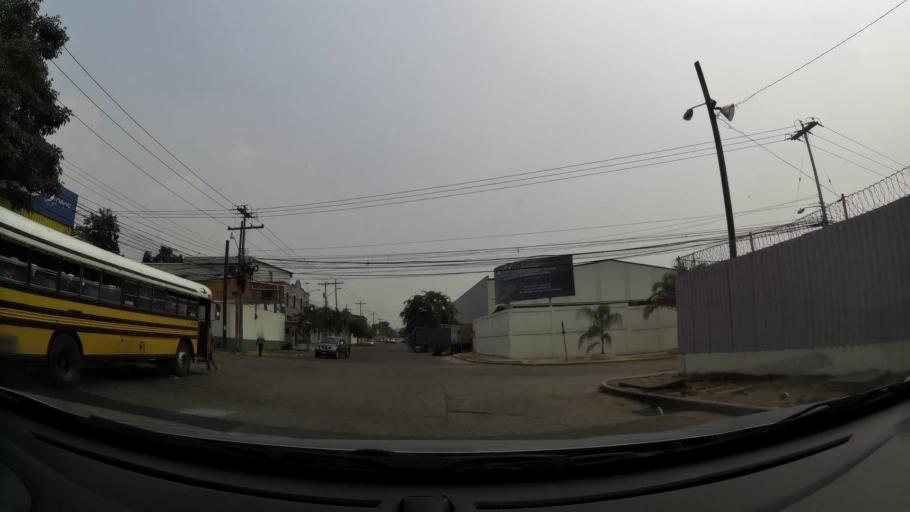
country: HN
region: Cortes
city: San Pedro Sula
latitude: 15.4887
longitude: -88.0299
